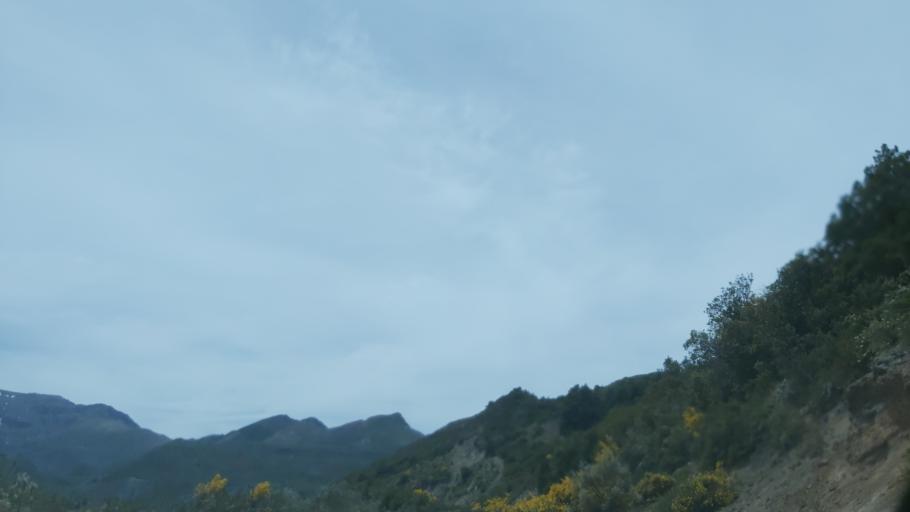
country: AR
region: Neuquen
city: Andacollo
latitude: -37.3919
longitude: -71.4036
